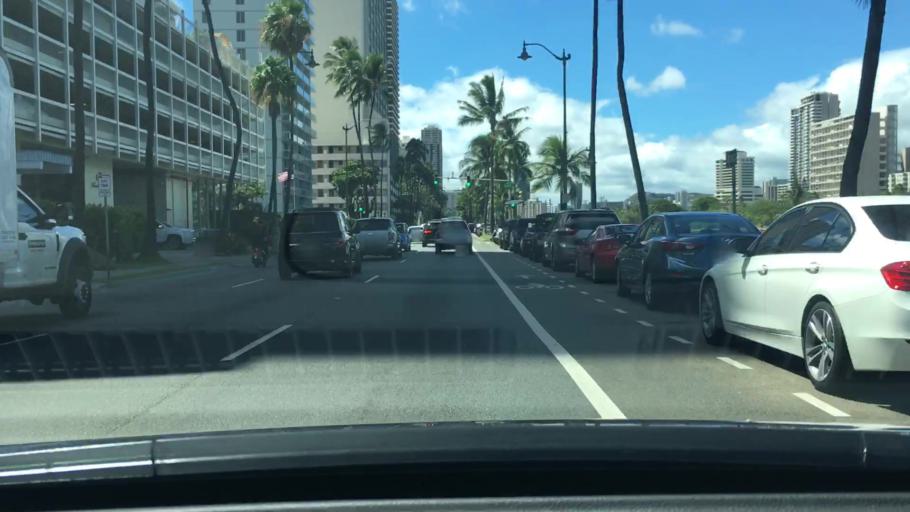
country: US
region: Hawaii
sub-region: Honolulu County
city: Honolulu
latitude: 21.2811
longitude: -157.8252
